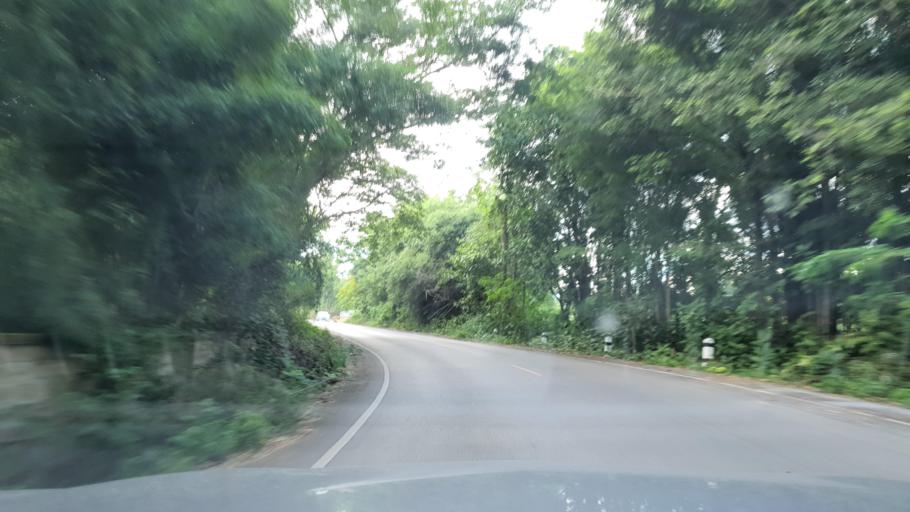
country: TH
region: Phayao
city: Phayao
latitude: 19.0982
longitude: 99.8297
